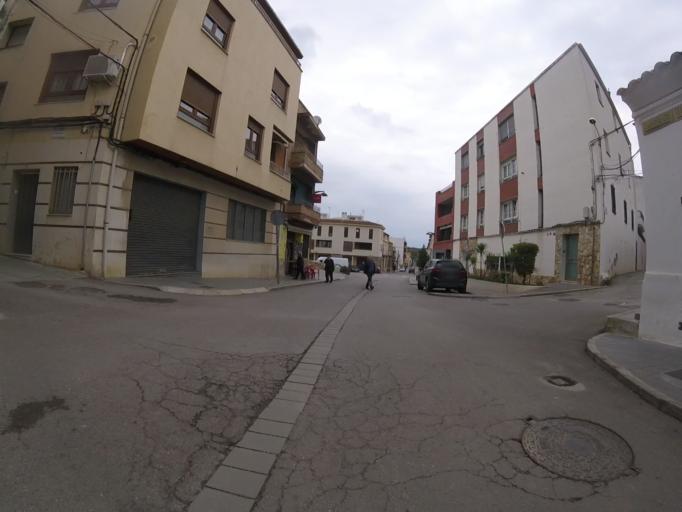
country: ES
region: Valencia
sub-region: Provincia de Castello
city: Cuevas de Vinroma
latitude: 40.3115
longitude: 0.1213
